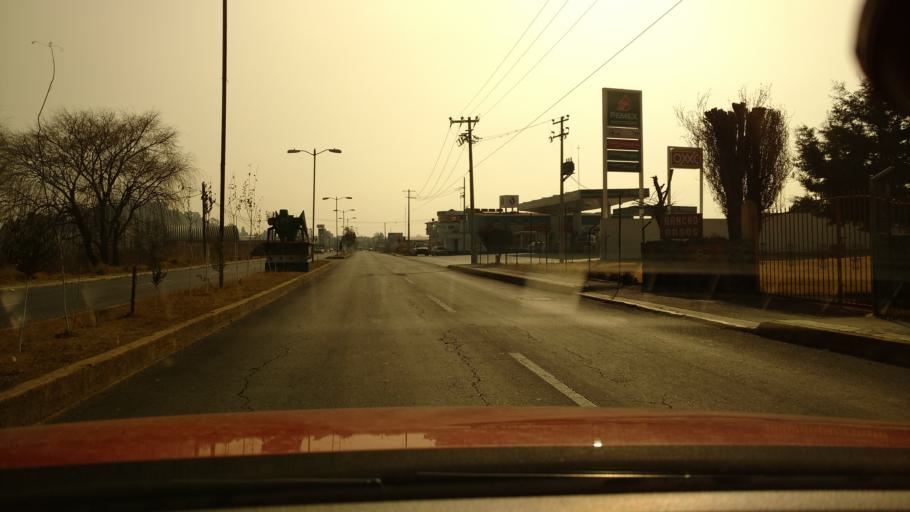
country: MX
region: Morelos
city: Chapultepec
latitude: 19.2044
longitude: -99.5700
